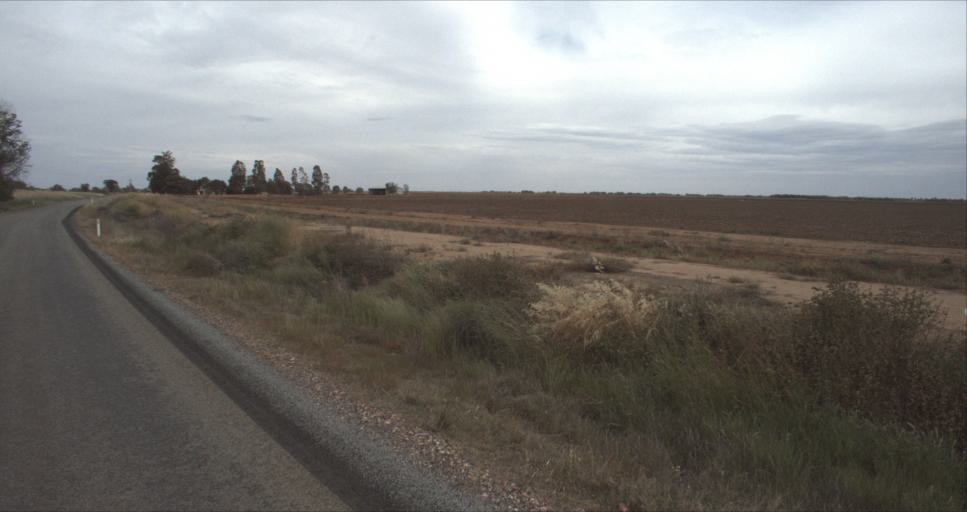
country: AU
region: New South Wales
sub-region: Leeton
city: Leeton
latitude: -34.4287
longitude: 146.3779
